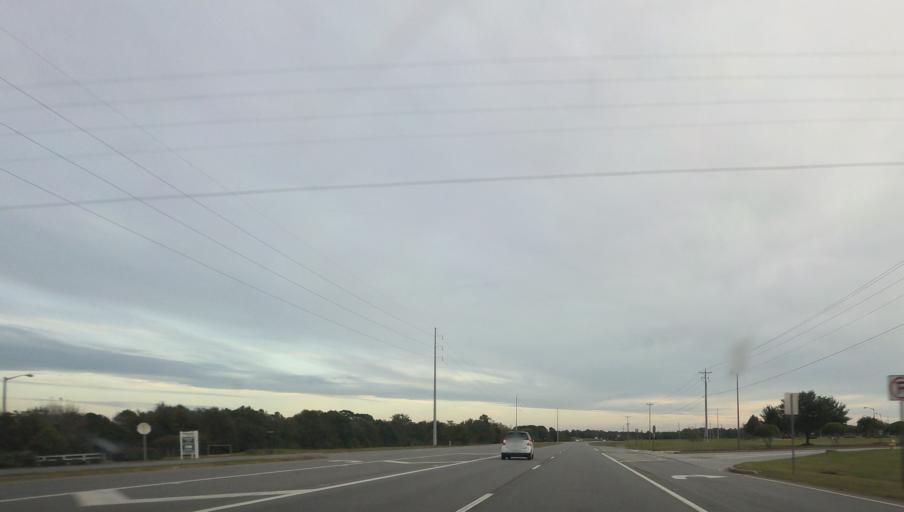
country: US
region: Georgia
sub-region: Houston County
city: Perry
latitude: 32.4699
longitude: -83.7005
